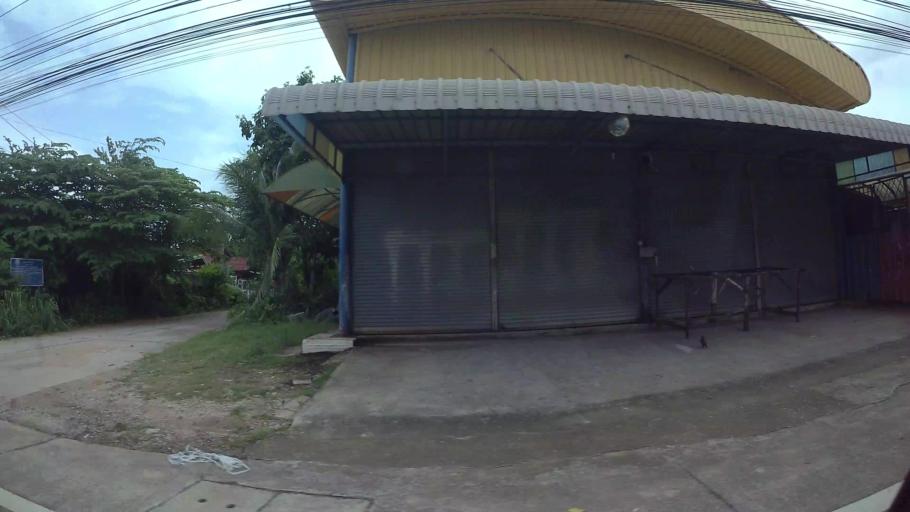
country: TH
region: Chon Buri
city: Si Racha
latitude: 13.1684
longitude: 100.9738
